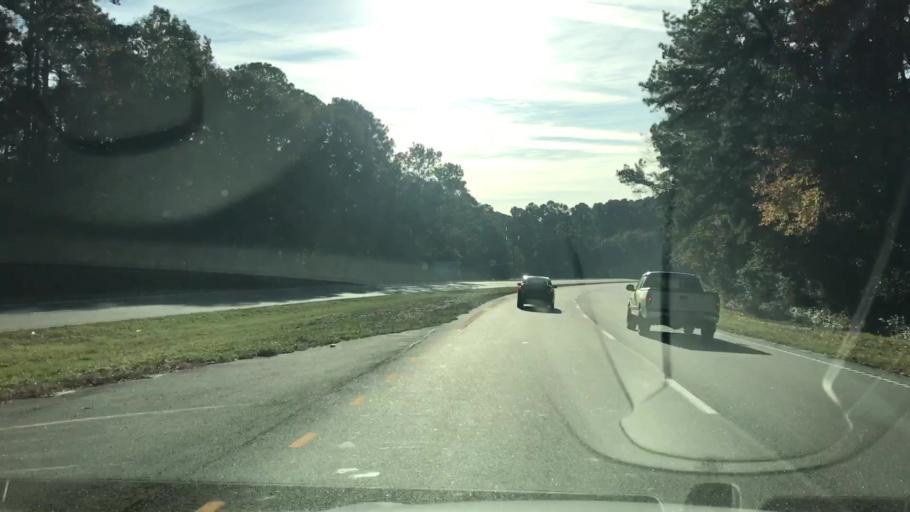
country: US
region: South Carolina
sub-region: Beaufort County
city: Laurel Bay
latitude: 32.5871
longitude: -80.7448
